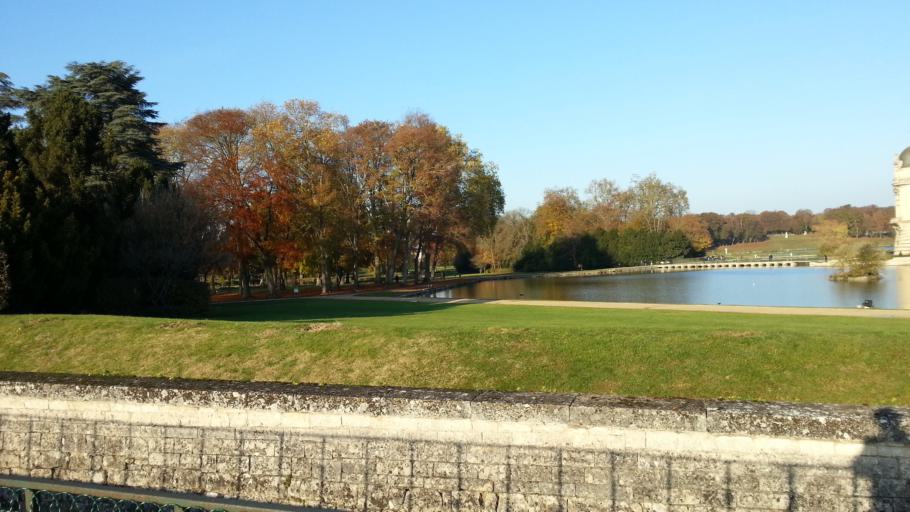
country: FR
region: Picardie
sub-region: Departement de l'Oise
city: Chantilly
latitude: 49.1931
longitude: 2.4831
